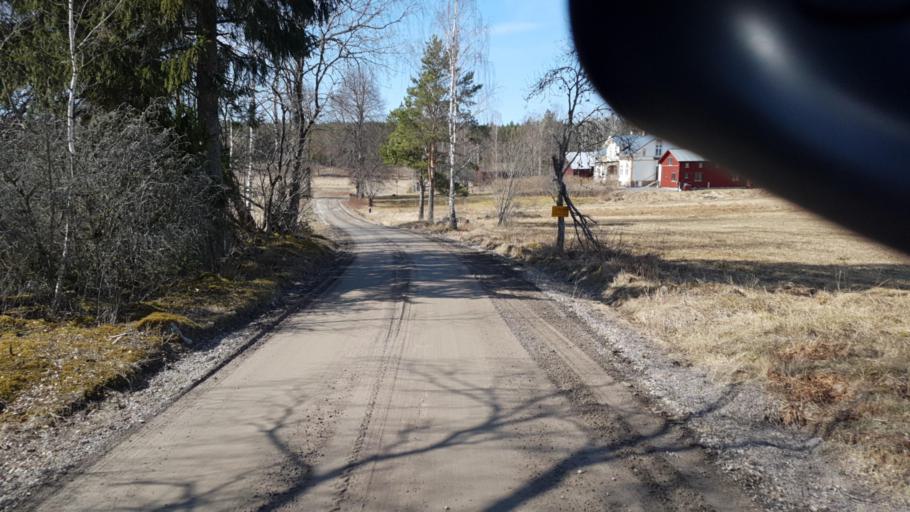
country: SE
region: Vaermland
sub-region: Grums Kommun
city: Grums
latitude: 59.4879
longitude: 12.9324
